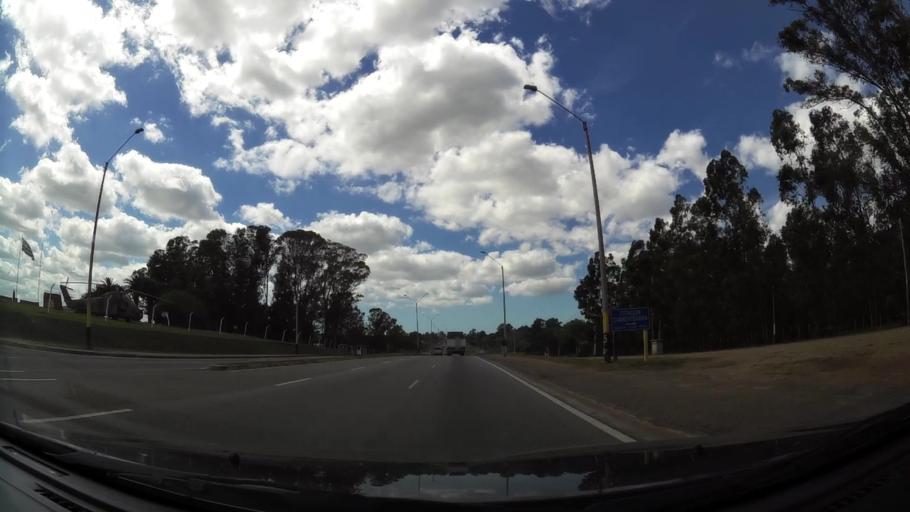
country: UY
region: Canelones
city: Colonia Nicolich
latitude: -34.8083
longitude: -56.0448
